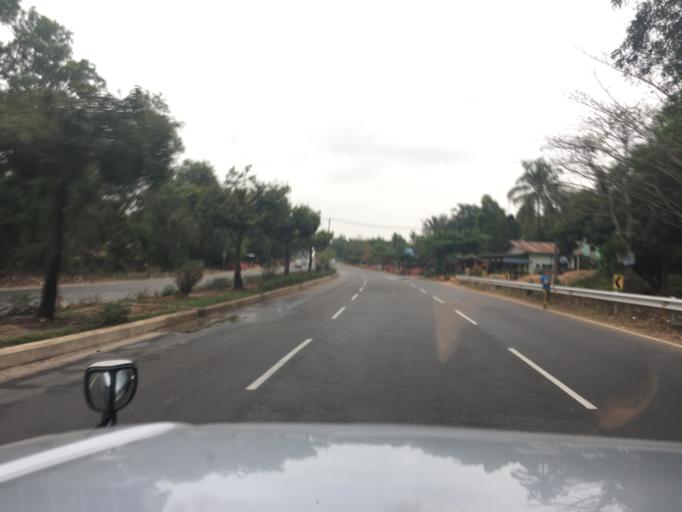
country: MM
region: Bago
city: Bago
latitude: 17.2344
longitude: 96.4614
